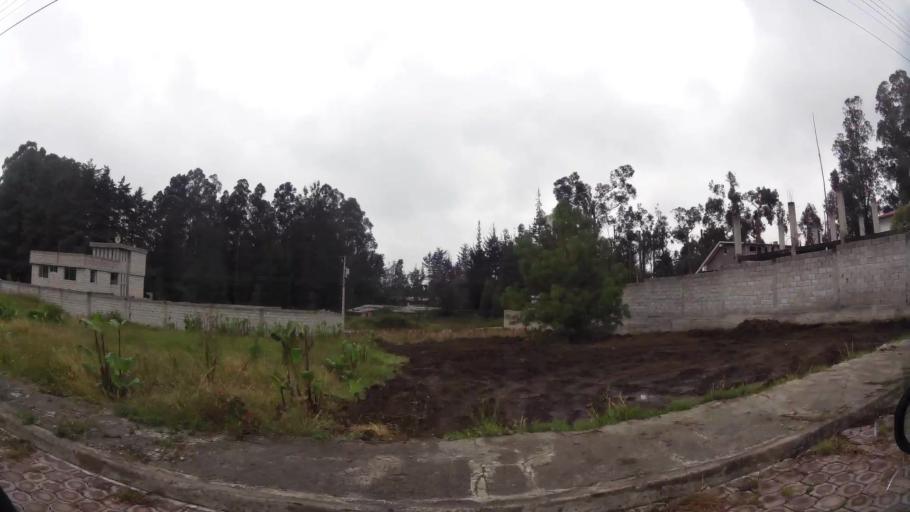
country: EC
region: Pichincha
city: Quito
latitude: -0.2691
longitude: -78.4735
